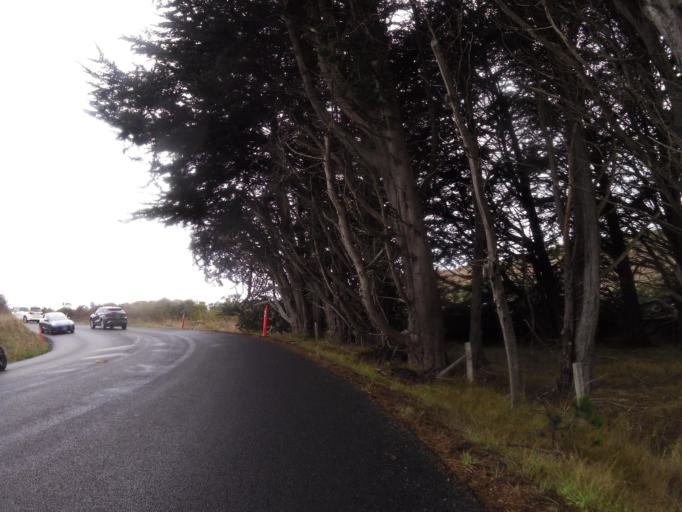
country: US
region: California
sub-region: Sonoma County
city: Monte Rio
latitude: 38.4318
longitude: -123.1083
